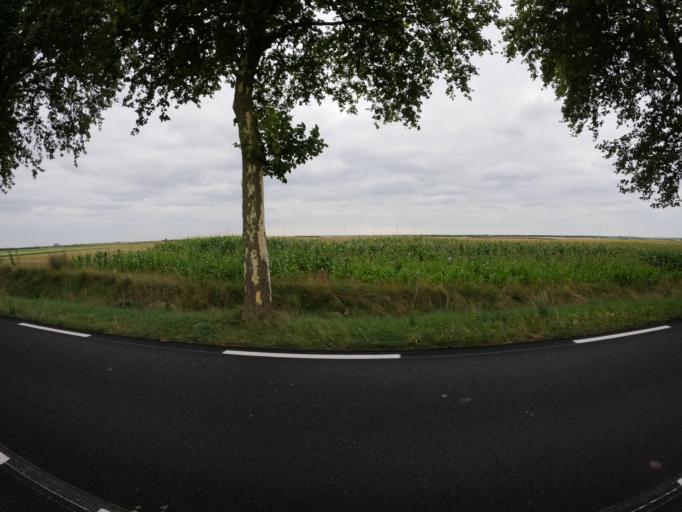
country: FR
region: Pays de la Loire
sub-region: Departement de la Vendee
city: Saint-Martin-sous-Mouzeuil
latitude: 46.5149
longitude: -0.9686
